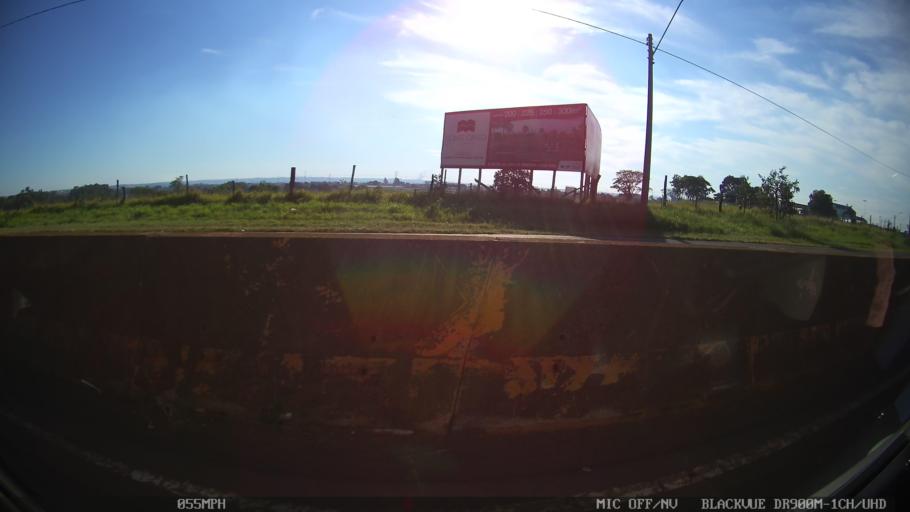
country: BR
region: Sao Paulo
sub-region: Americo Brasiliense
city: Americo Brasiliense
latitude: -21.7494
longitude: -48.1344
